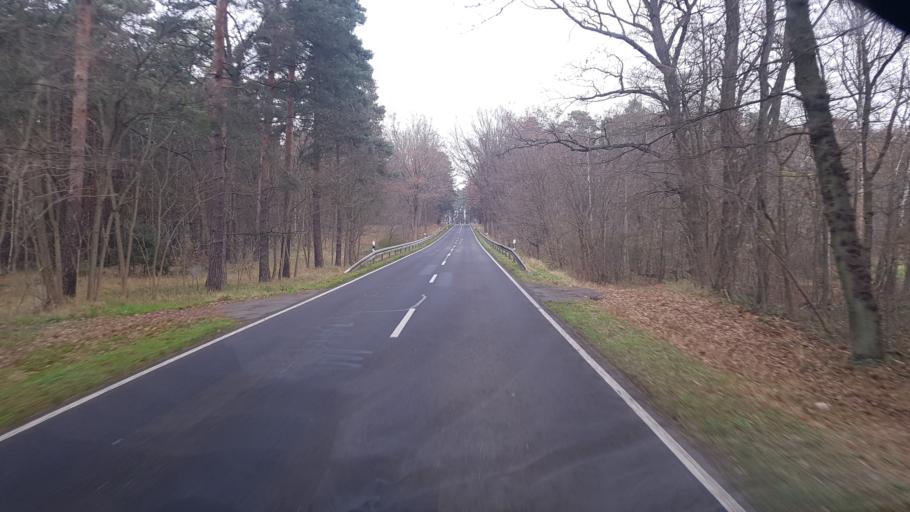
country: DE
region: Brandenburg
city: Schenkendobern
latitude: 51.9446
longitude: 14.6333
